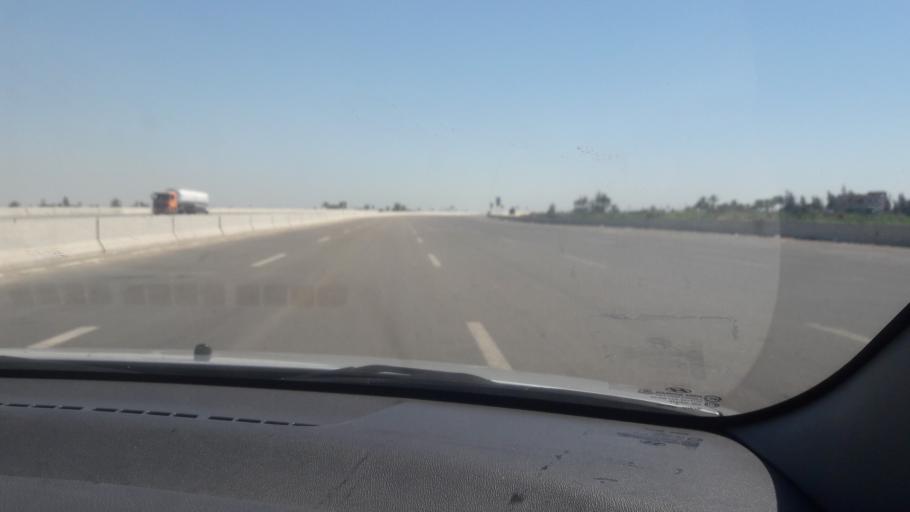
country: EG
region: Muhafazat Bur Sa`id
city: Port Said
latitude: 31.1103
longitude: 32.2340
